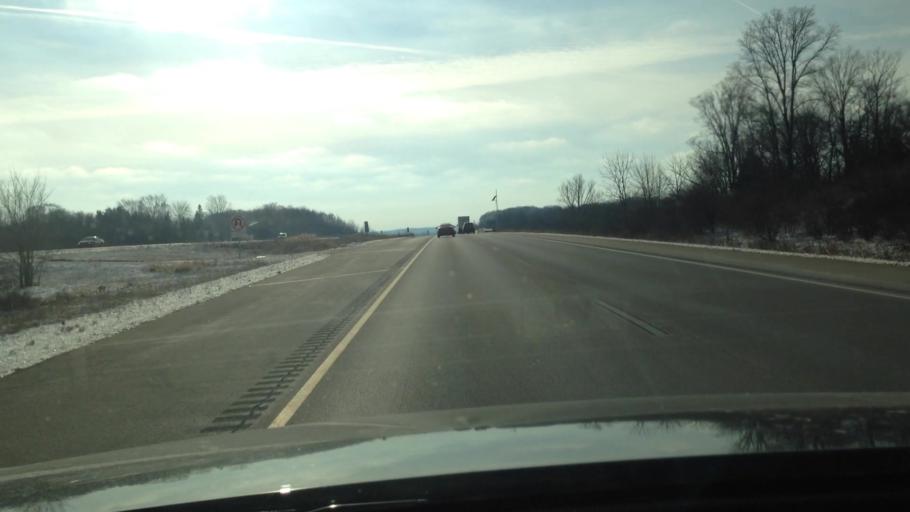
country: US
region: Wisconsin
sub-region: Waukesha County
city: Big Bend
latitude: 42.8882
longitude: -88.2709
